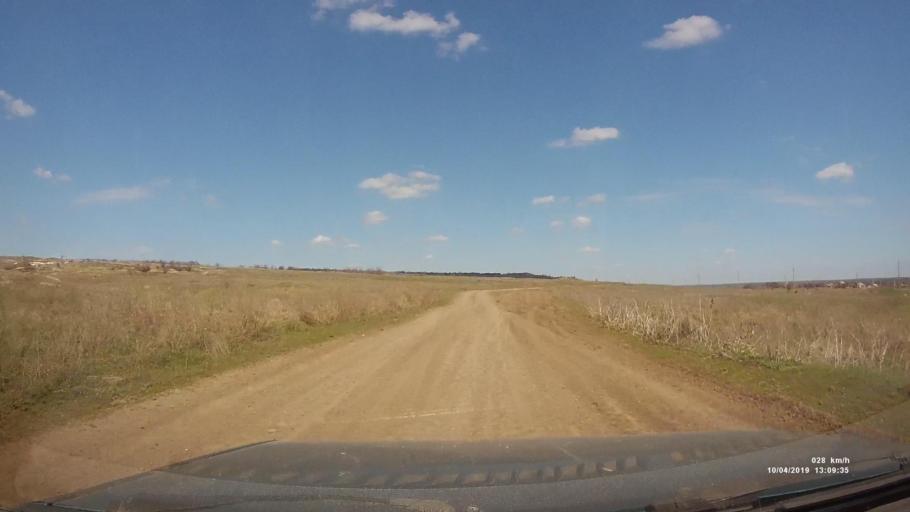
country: RU
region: Rostov
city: Masalovka
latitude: 48.4068
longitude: 40.2439
